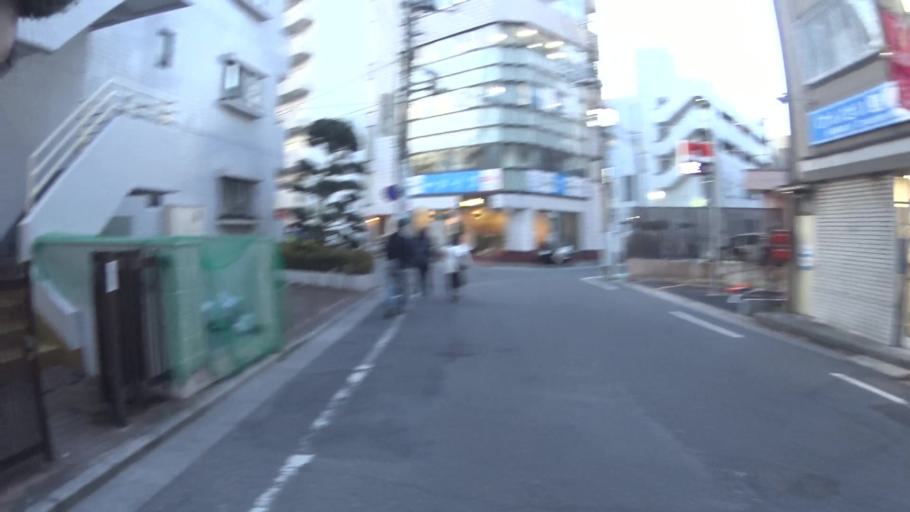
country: JP
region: Saitama
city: Shimotoda
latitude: 35.8479
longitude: 139.6721
